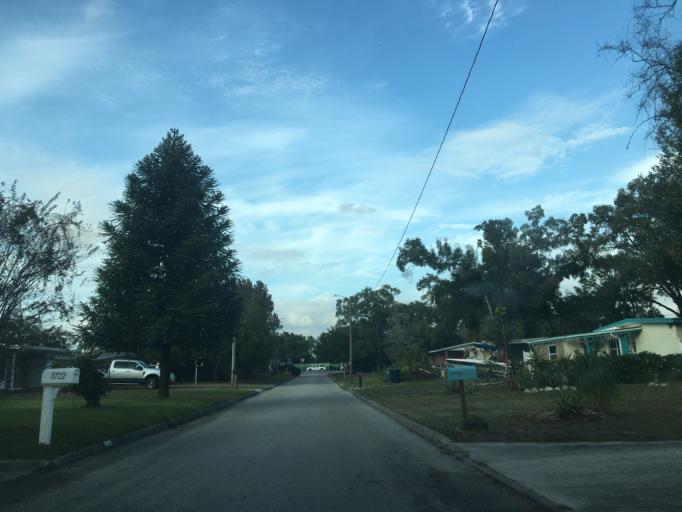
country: US
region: Florida
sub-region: Hillsborough County
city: Temple Terrace
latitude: 28.0312
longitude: -82.4187
